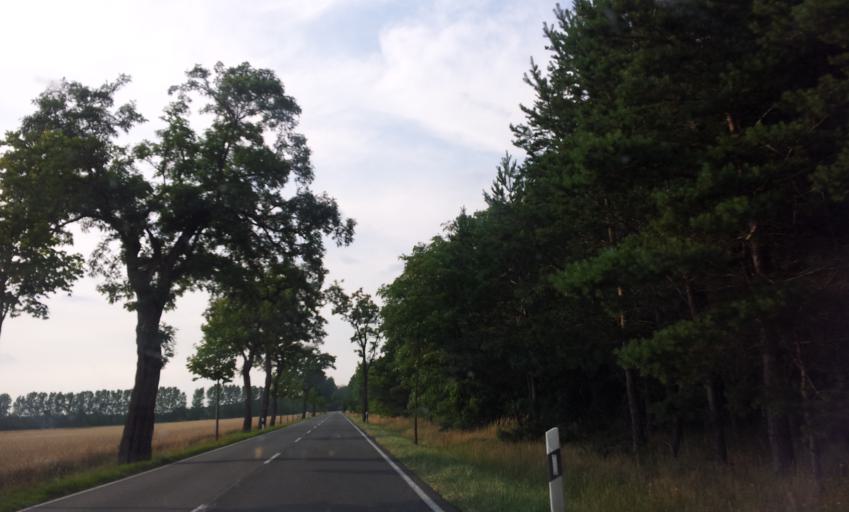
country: DE
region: Brandenburg
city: Beelitz
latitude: 52.1252
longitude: 13.0138
